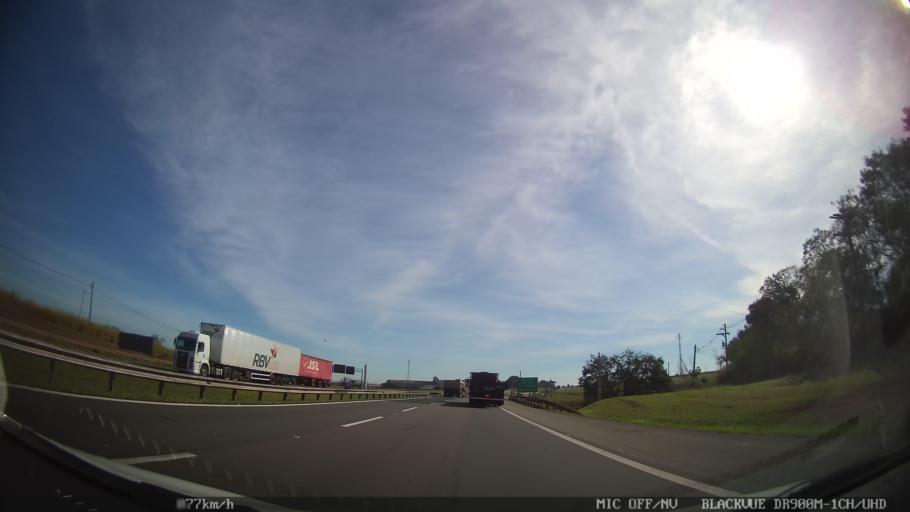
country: BR
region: Sao Paulo
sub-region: Limeira
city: Limeira
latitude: -22.5050
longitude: -47.4004
